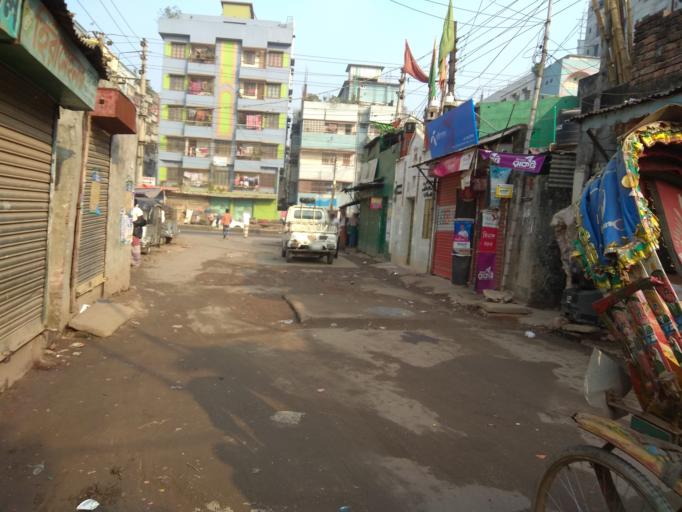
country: BD
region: Dhaka
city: Tungi
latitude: 23.8204
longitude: 90.3682
